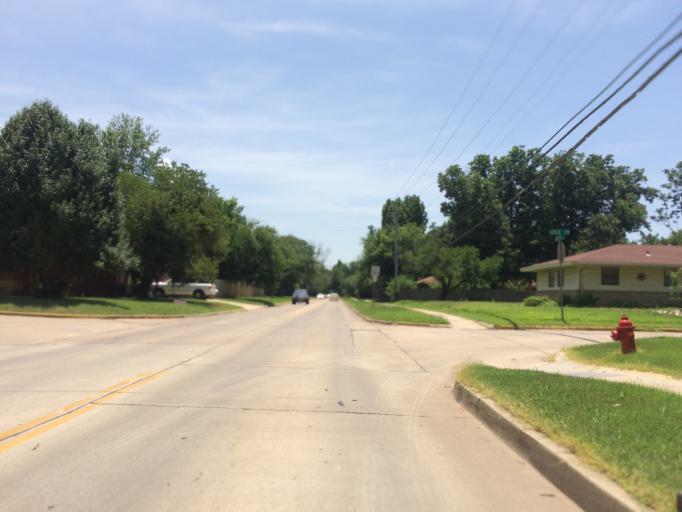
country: US
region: Oklahoma
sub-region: Cleveland County
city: Norman
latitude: 35.2104
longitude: -97.4590
